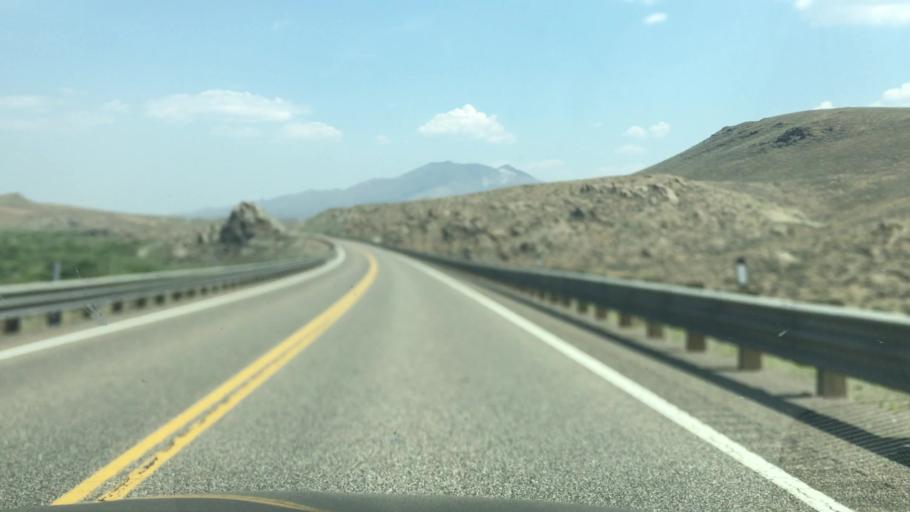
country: US
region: Nevada
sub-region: Elko County
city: Jackpot
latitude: 41.7432
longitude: -114.7737
